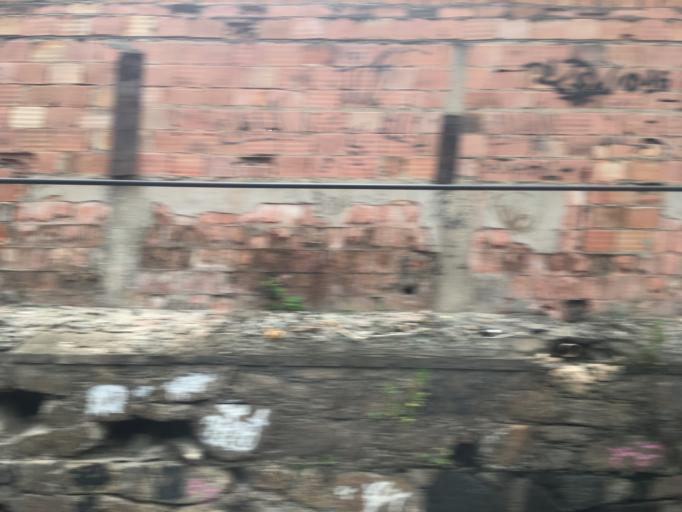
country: BR
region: Rio de Janeiro
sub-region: Rio De Janeiro
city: Rio de Janeiro
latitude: -22.9019
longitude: -43.2602
